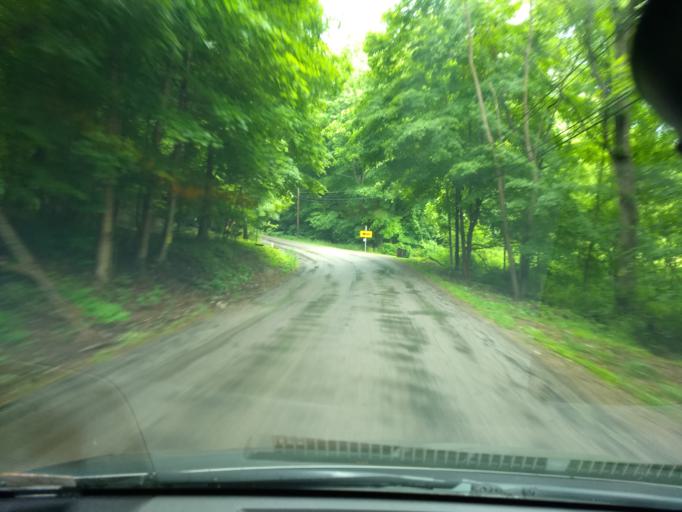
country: US
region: Pennsylvania
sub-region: Westmoreland County
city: Avonmore
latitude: 40.5322
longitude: -79.4912
